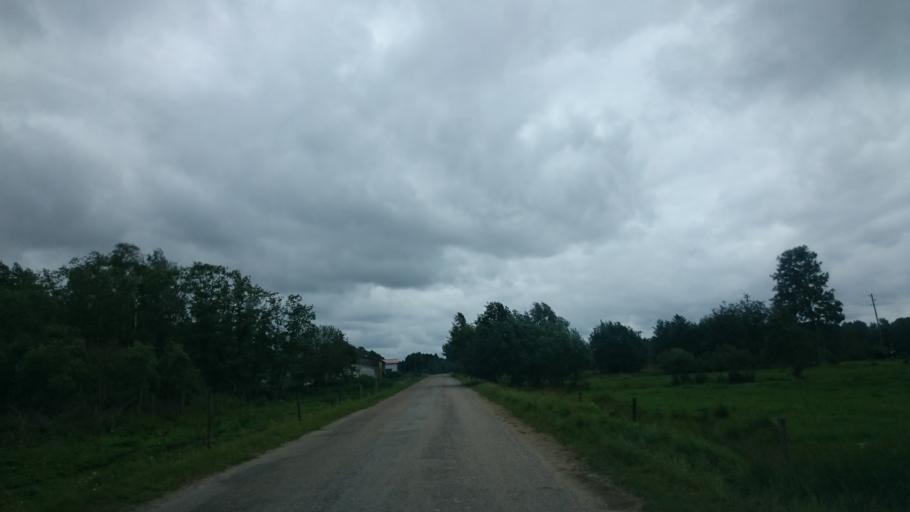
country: LV
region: Durbe
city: Liegi
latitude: 56.7479
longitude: 21.3664
